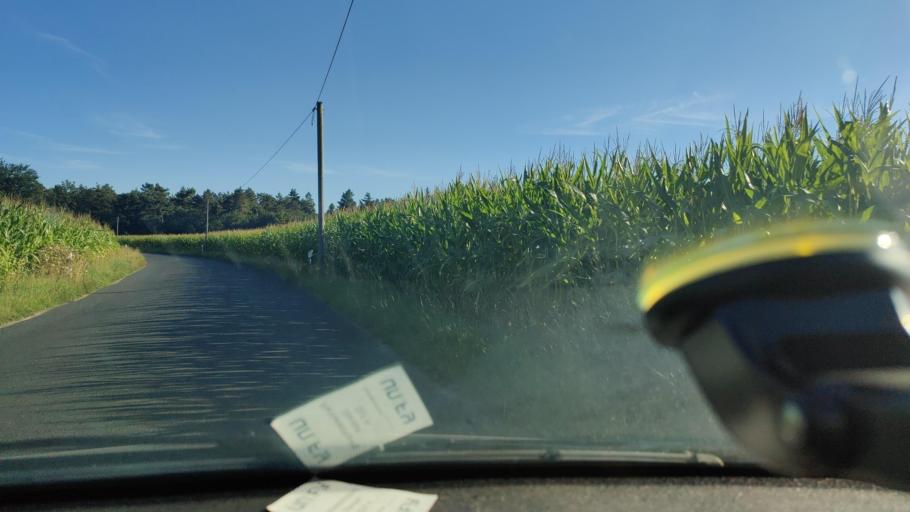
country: DE
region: North Rhine-Westphalia
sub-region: Regierungsbezirk Dusseldorf
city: Goch
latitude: 51.6678
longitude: 6.0815
